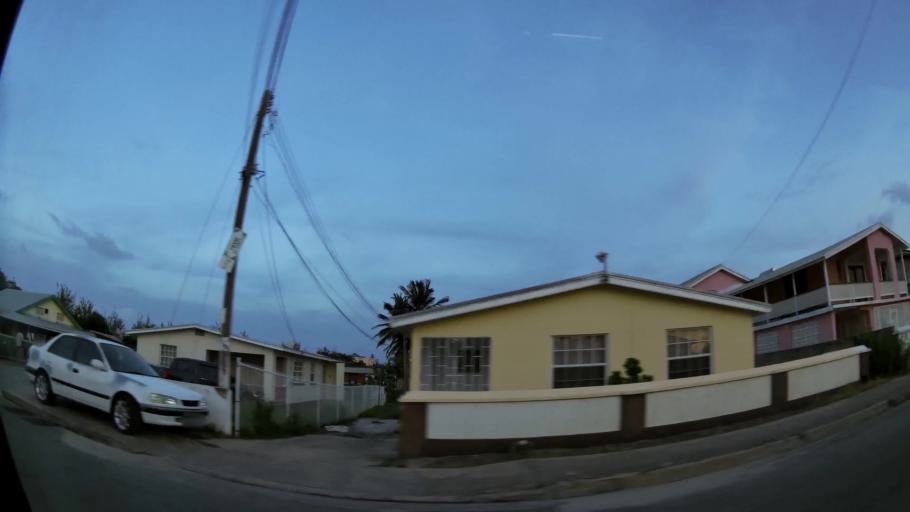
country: BB
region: Saint Philip
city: Crane
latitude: 13.1048
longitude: -59.4486
